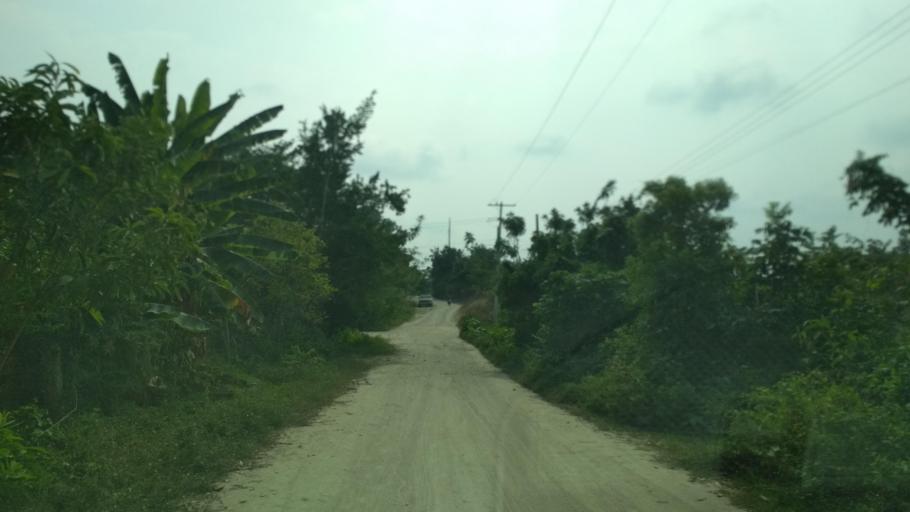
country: MM
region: Kayah
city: Loikaw
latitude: 20.2151
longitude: 97.2849
